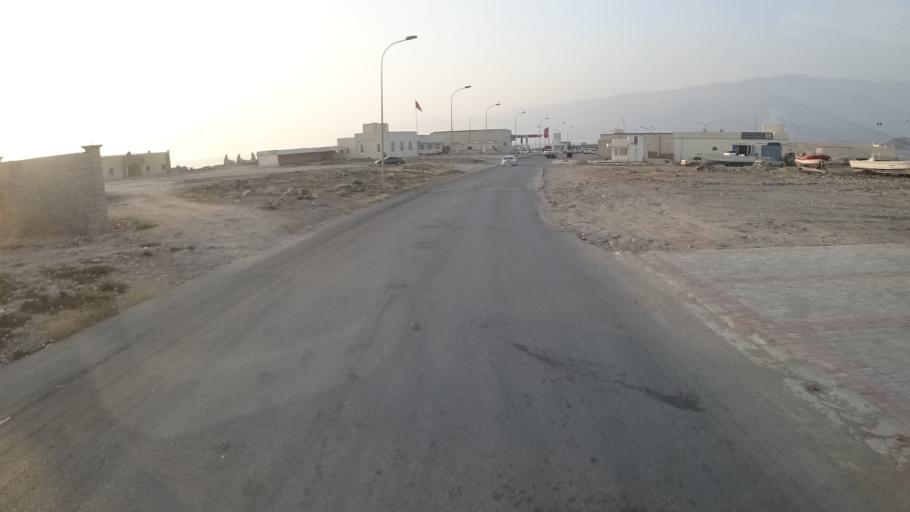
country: OM
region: Zufar
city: Salalah
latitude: 16.9841
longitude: 54.6878
